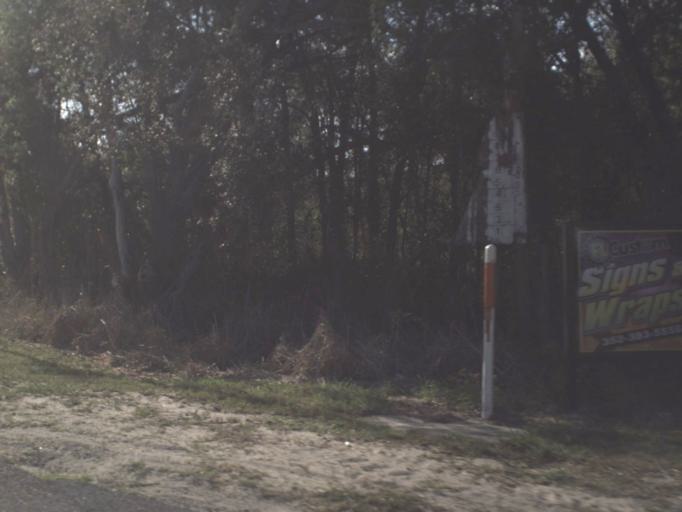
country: US
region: Florida
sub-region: Lake County
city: Mount Plymouth
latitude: 28.8080
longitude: -81.5437
